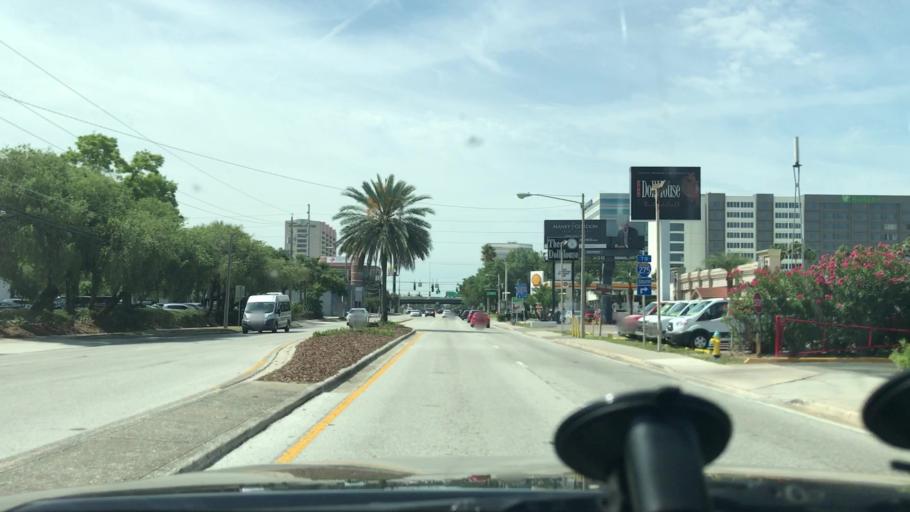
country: US
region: Florida
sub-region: Hillsborough County
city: Tampa
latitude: 27.9537
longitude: -82.5242
